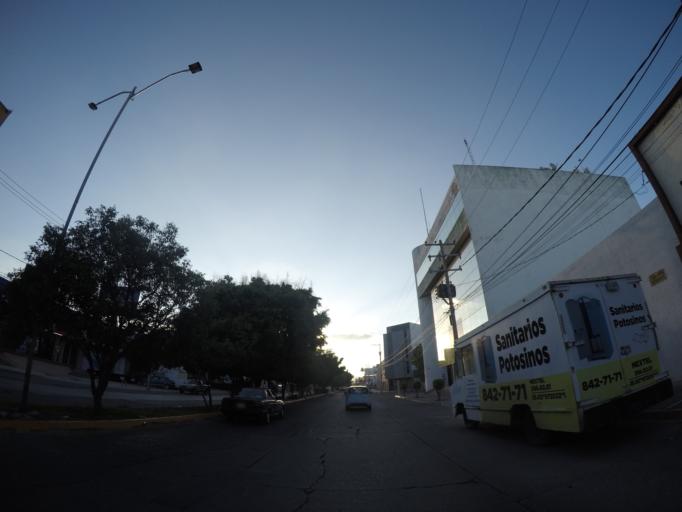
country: MX
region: San Luis Potosi
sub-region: San Luis Potosi
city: San Luis Potosi
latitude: 22.1419
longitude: -100.9974
